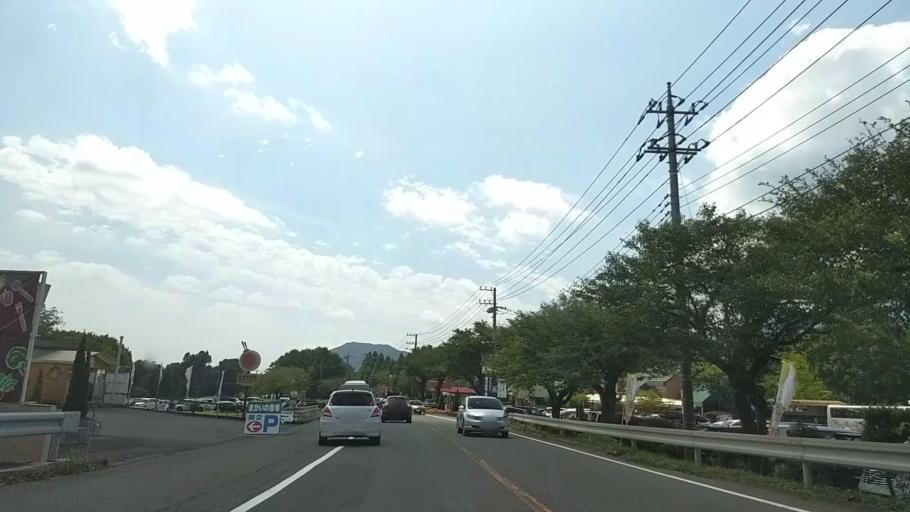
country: JP
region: Shizuoka
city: Fujinomiya
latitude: 35.3370
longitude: 138.5851
